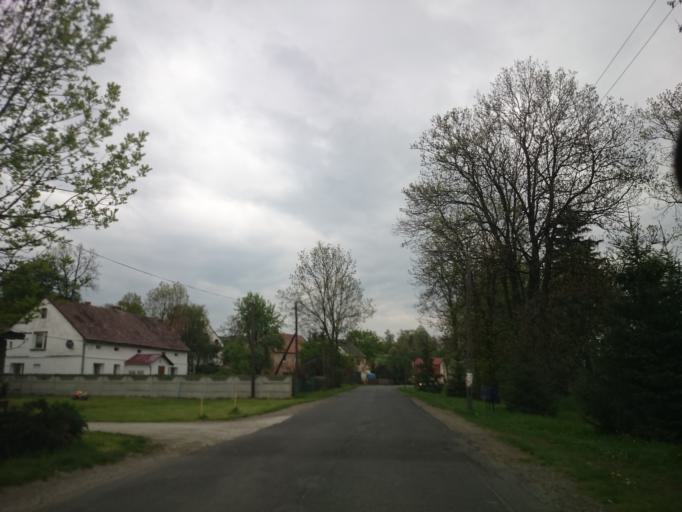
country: PL
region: Lower Silesian Voivodeship
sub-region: Powiat klodzki
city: Klodzko
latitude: 50.4210
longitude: 16.6793
